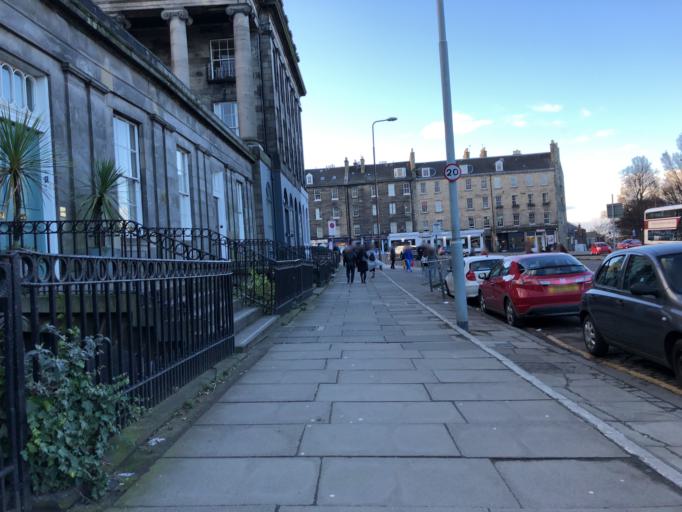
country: GB
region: Scotland
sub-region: Edinburgh
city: Edinburgh
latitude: 55.9576
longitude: -3.1835
